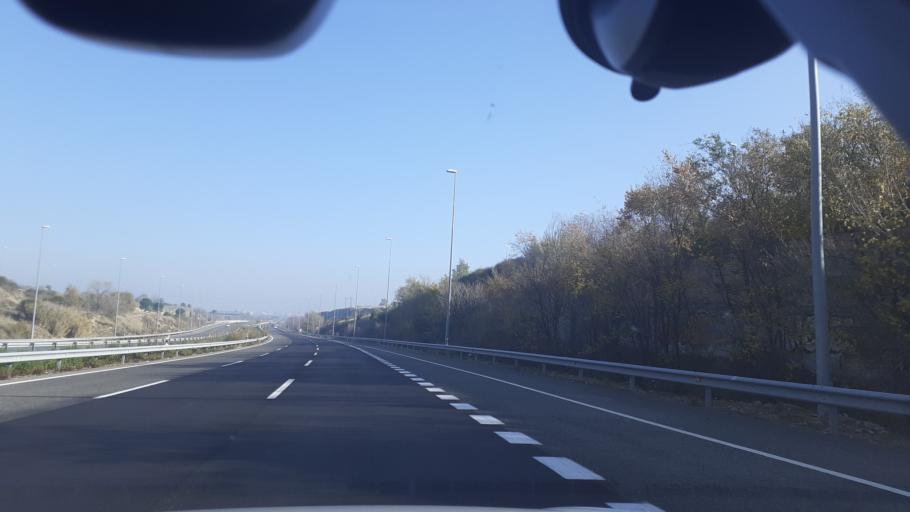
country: ES
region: Madrid
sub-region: Provincia de Madrid
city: Vicalvaro
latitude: 40.4127
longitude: -3.6089
